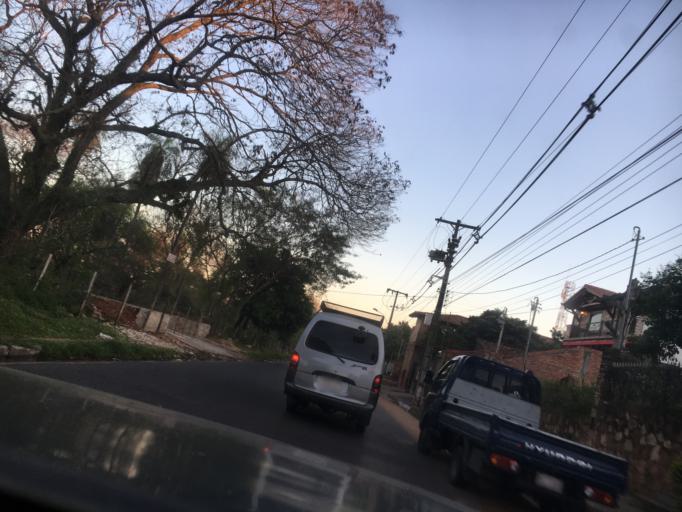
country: PY
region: Central
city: Lambare
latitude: -25.3474
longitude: -57.6013
